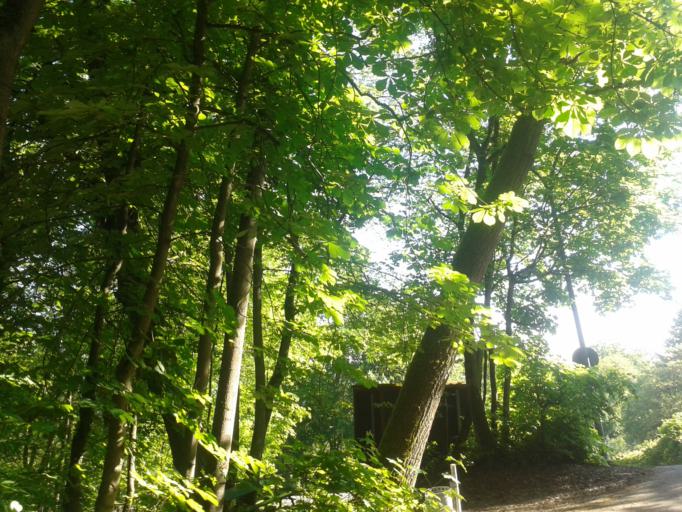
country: DE
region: Bavaria
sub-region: Upper Franconia
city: Stegaurach
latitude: 49.8819
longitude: 10.8701
